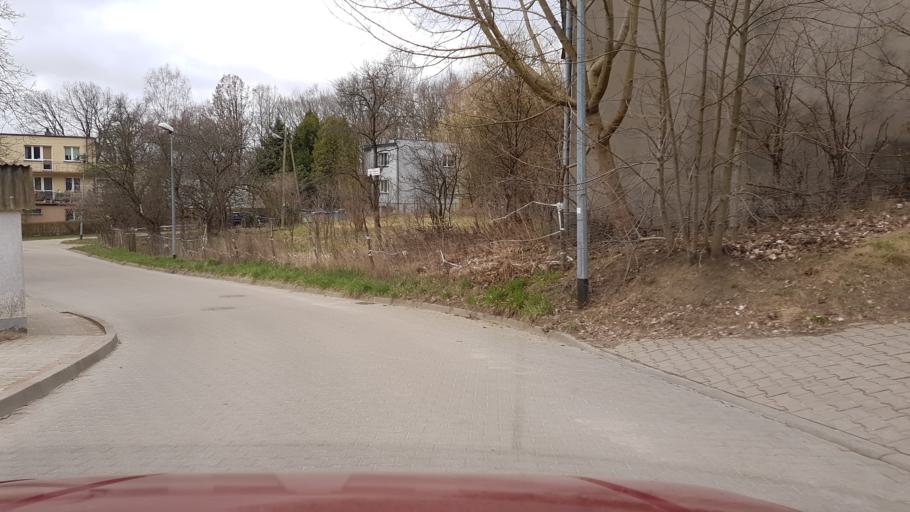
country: PL
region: West Pomeranian Voivodeship
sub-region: Powiat koszalinski
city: Sianow
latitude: 54.1904
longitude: 16.2425
